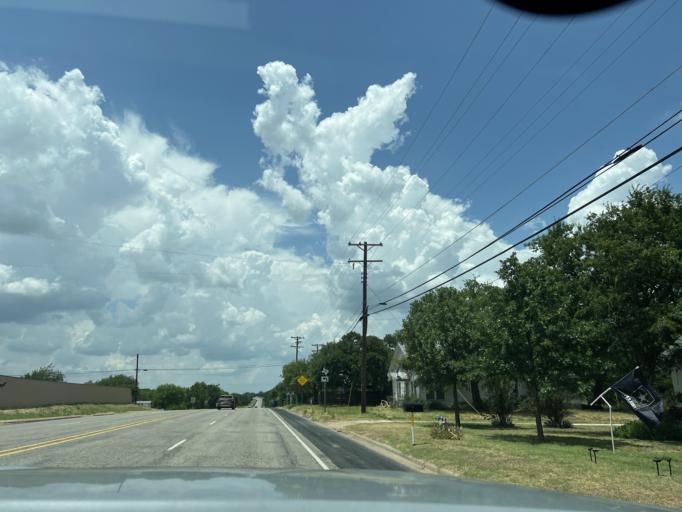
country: US
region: Texas
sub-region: Palo Pinto County
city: Palo Pinto
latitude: 32.7681
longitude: -98.3033
